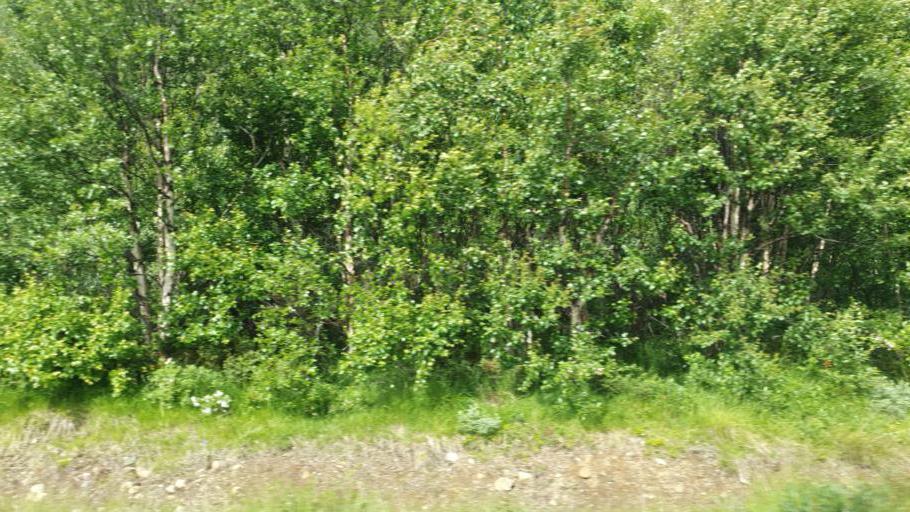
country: NO
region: Oppland
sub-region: Vaga
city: Vagamo
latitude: 61.5271
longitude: 8.8761
